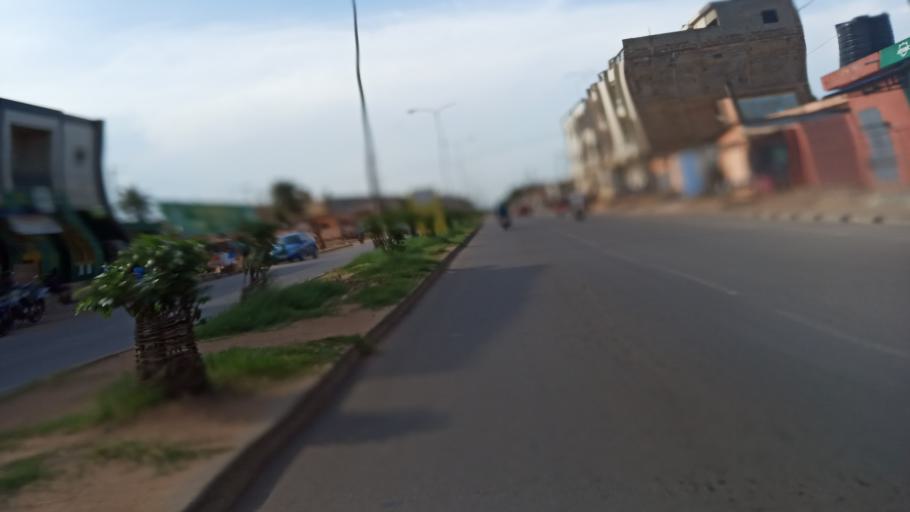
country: TG
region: Maritime
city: Lome
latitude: 6.1692
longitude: 1.2670
